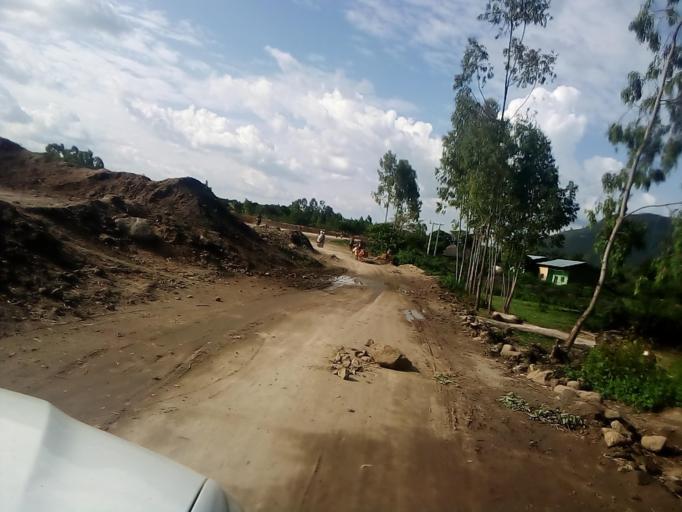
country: ET
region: Southern Nations, Nationalities, and People's Region
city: K'olito
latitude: 7.6190
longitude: 38.0640
